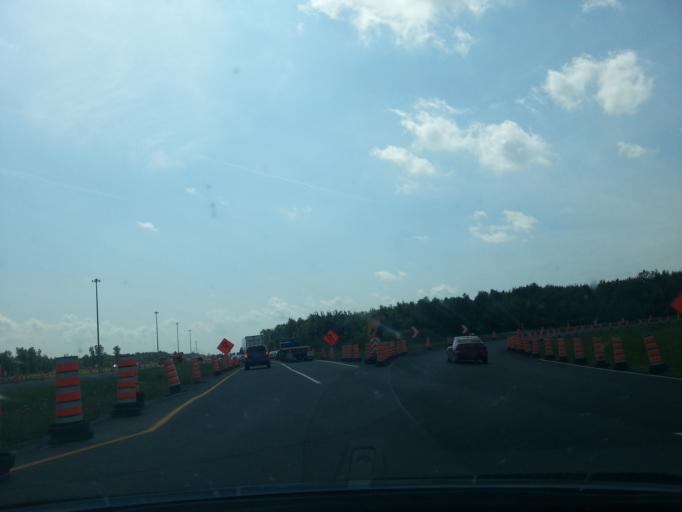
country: CA
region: Quebec
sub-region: Mauricie
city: Saint-Germain-de-Grantham
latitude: 45.8768
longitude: -72.5552
